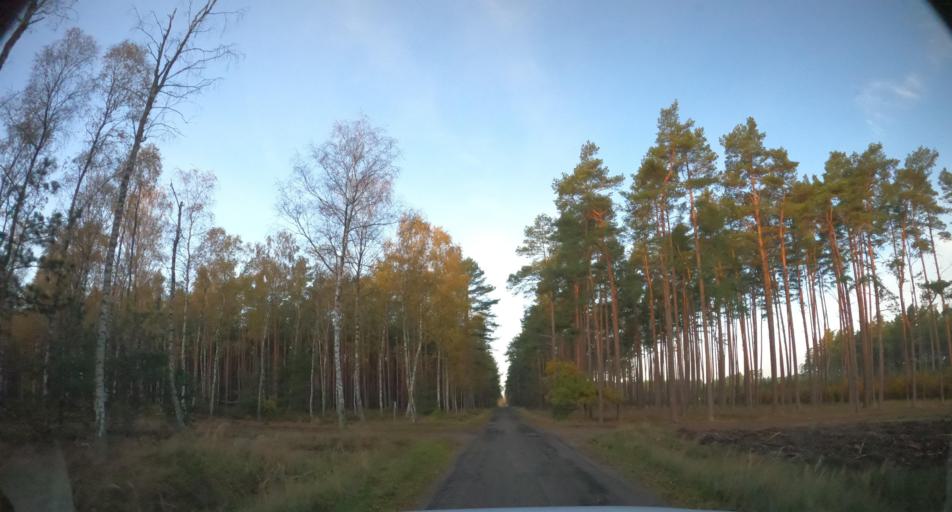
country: PL
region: West Pomeranian Voivodeship
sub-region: Powiat policki
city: Nowe Warpno
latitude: 53.6434
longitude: 14.3603
